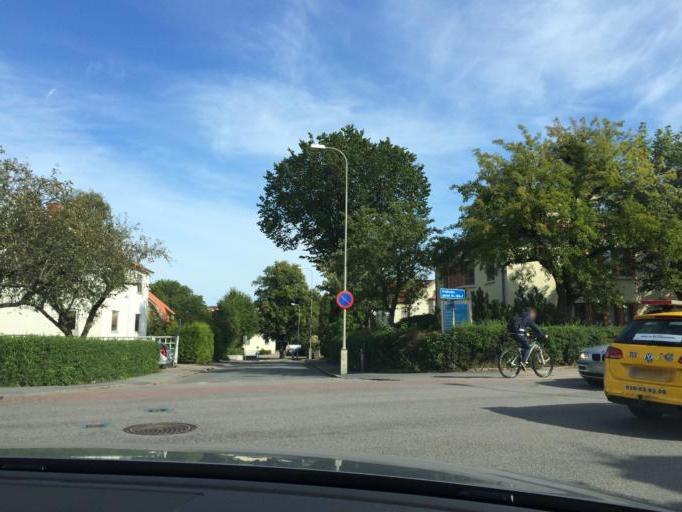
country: SE
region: Vaestra Goetaland
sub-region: Goteborg
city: Goeteborg
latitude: 57.6839
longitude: 11.9858
